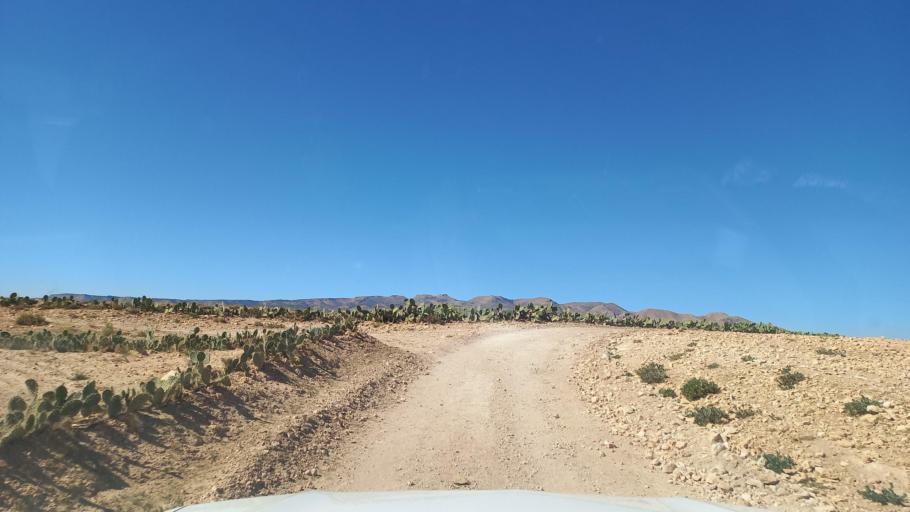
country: TN
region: Al Qasrayn
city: Sbiba
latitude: 35.3794
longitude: 9.0892
